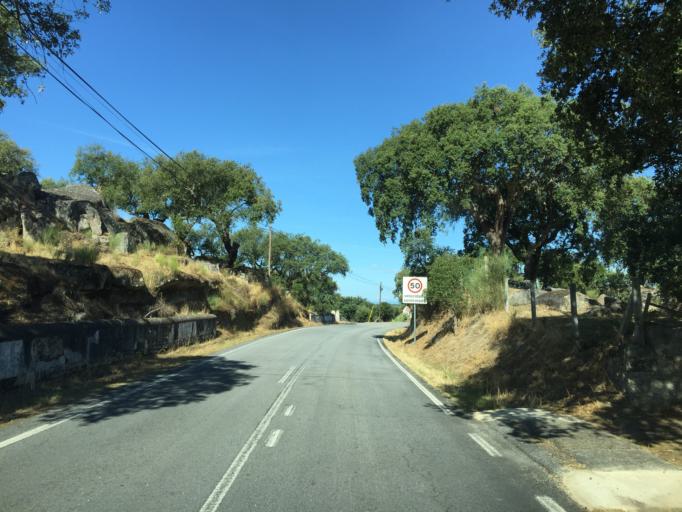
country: PT
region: Portalegre
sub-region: Marvao
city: Marvao
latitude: 39.4326
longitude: -7.3617
